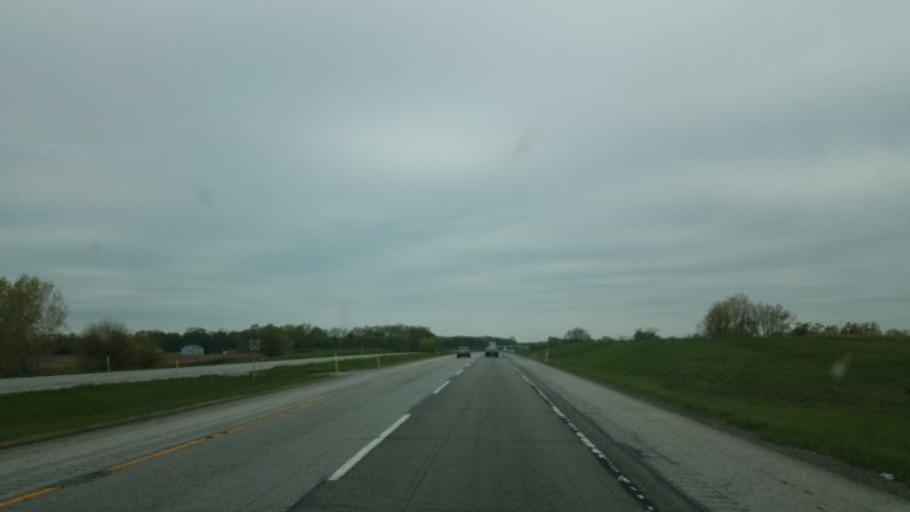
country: US
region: Michigan
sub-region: Saint Joseph County
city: White Pigeon
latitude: 41.7520
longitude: -85.6079
